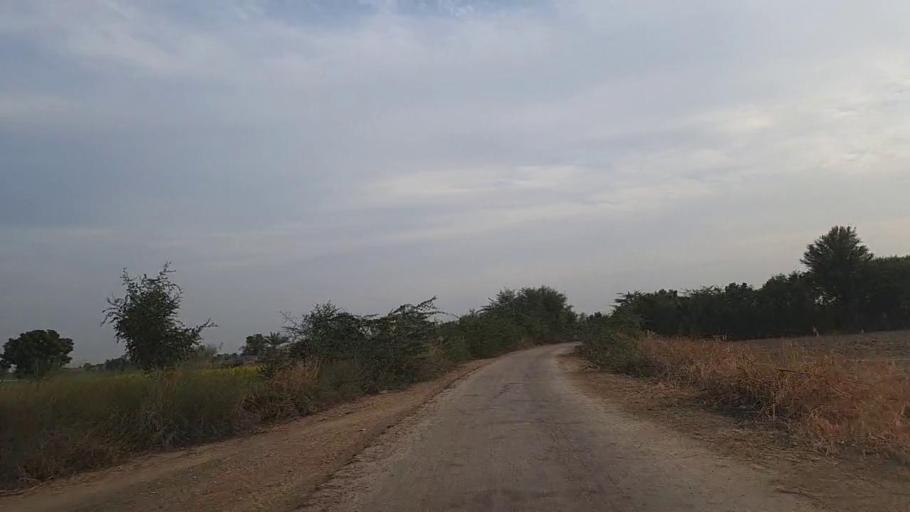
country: PK
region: Sindh
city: Jam Sahib
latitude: 26.4777
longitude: 68.5644
